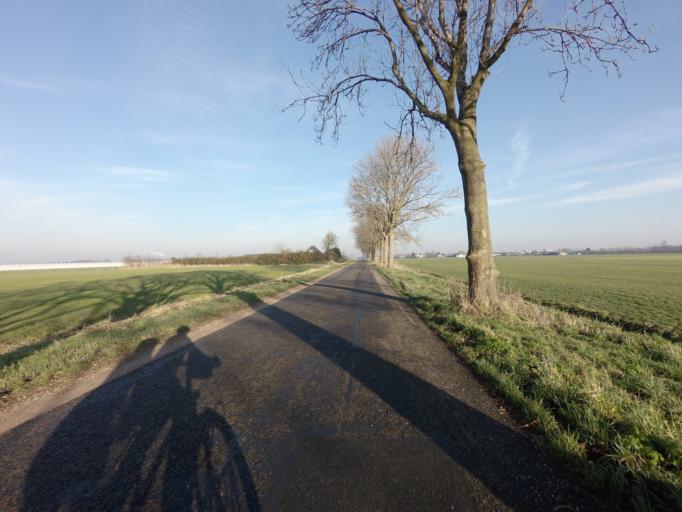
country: NL
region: Utrecht
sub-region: Gemeente De Ronde Venen
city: Mijdrecht
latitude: 52.2035
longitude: 4.8326
